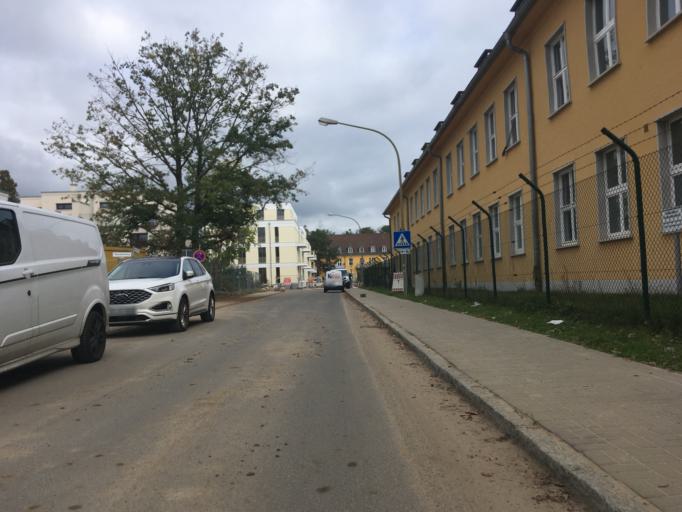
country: DE
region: Berlin
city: Kladow
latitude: 52.4656
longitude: 13.1573
